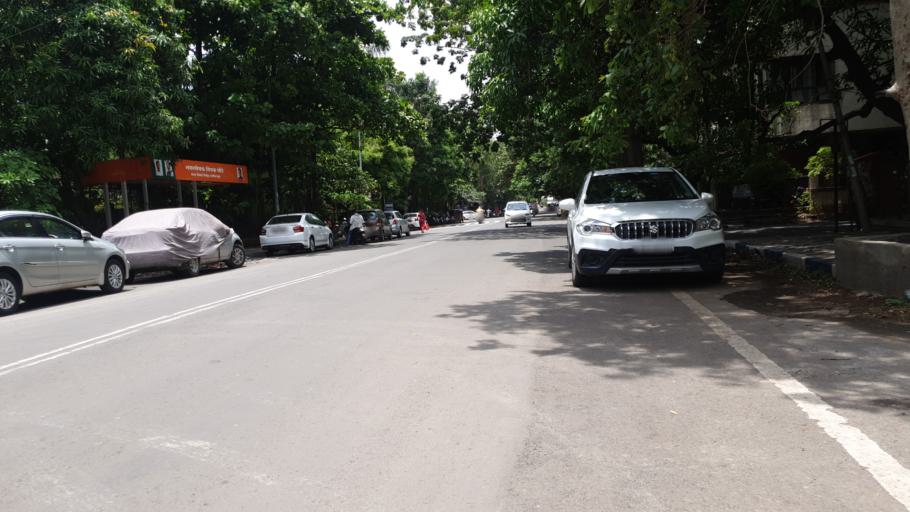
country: IN
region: Maharashtra
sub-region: Pune Division
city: Pune
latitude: 18.4930
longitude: 73.8267
